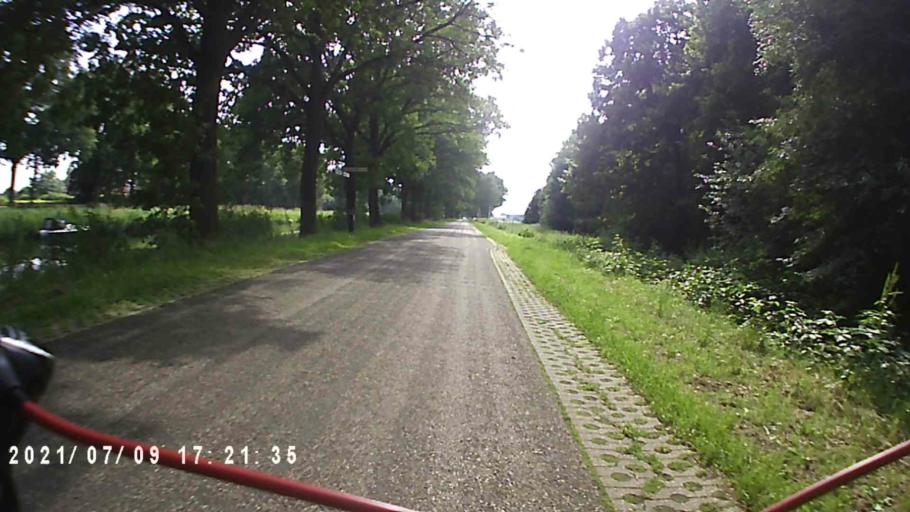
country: NL
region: Groningen
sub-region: Gemeente Vlagtwedde
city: Vlagtwedde
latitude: 53.0833
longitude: 7.1595
